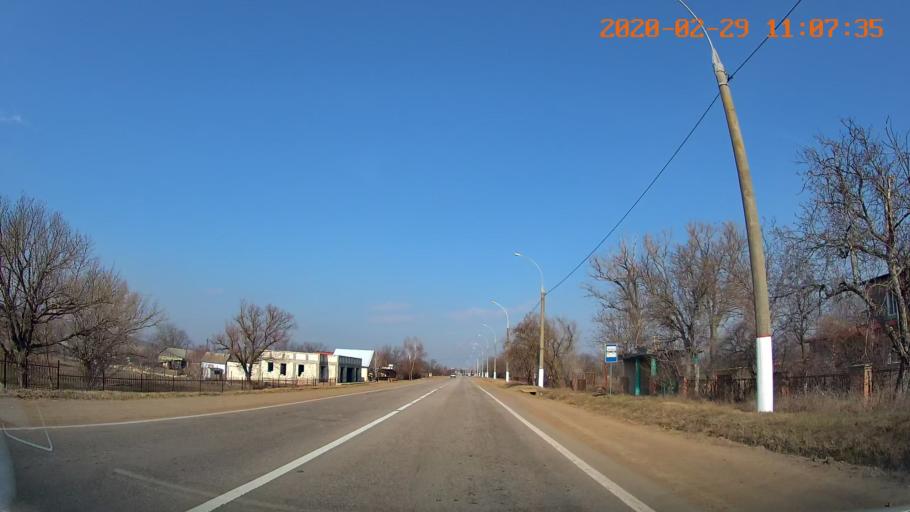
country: MD
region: Criuleni
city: Criuleni
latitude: 47.2266
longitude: 29.1811
